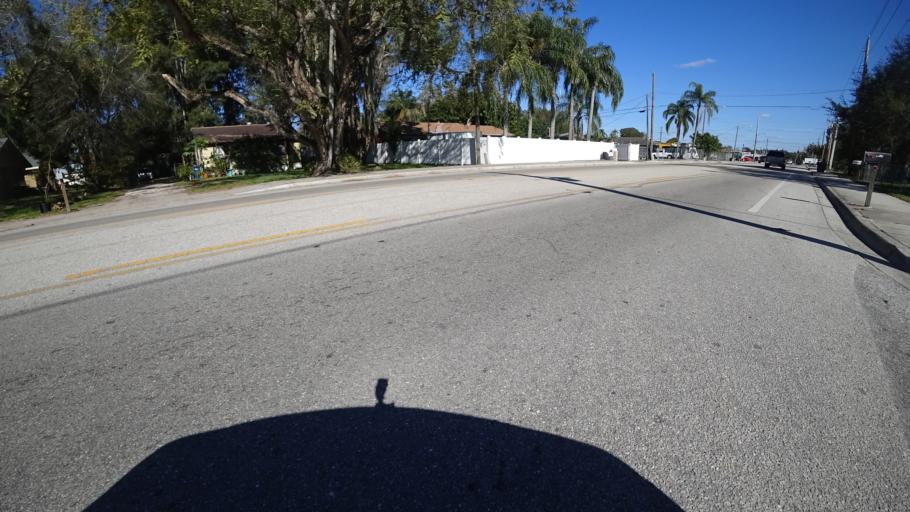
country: US
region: Florida
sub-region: Manatee County
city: West Samoset
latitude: 27.4402
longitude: -82.5492
